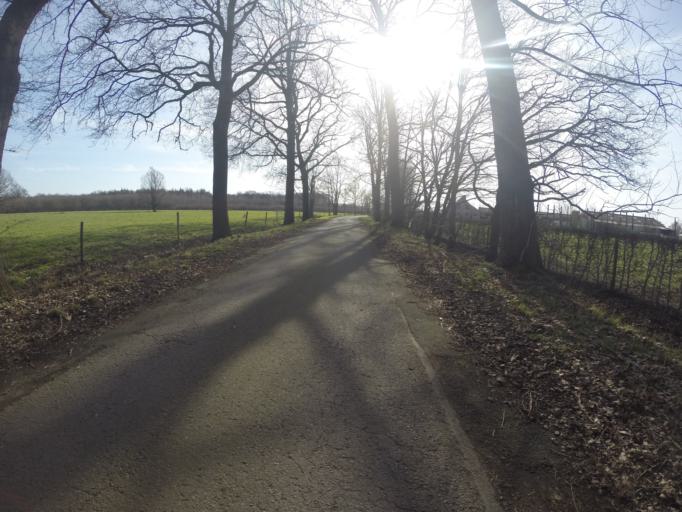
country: BE
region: Flanders
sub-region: Provincie West-Vlaanderen
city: Oostkamp
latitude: 51.1181
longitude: 3.2397
